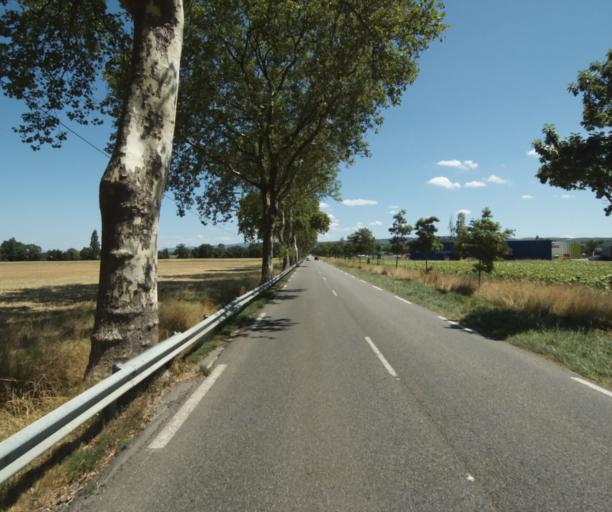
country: FR
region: Midi-Pyrenees
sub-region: Departement de la Haute-Garonne
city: Saint-Felix-Lauragais
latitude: 43.4466
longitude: 1.9400
